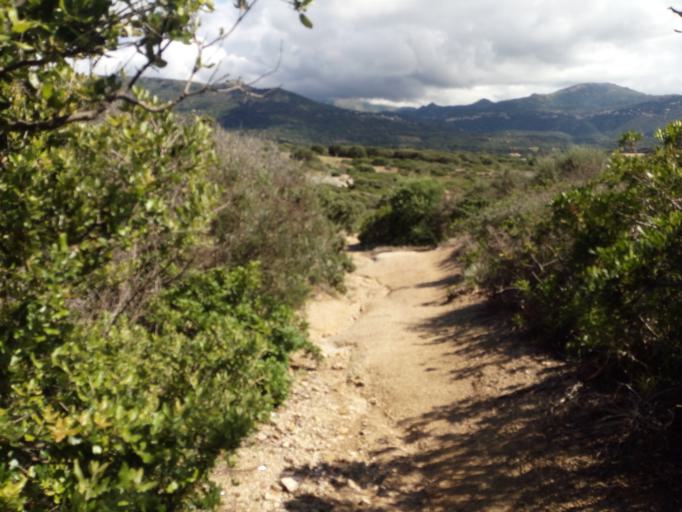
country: FR
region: Corsica
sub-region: Departement de la Haute-Corse
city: Lumio
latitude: 42.6176
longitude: 8.8780
